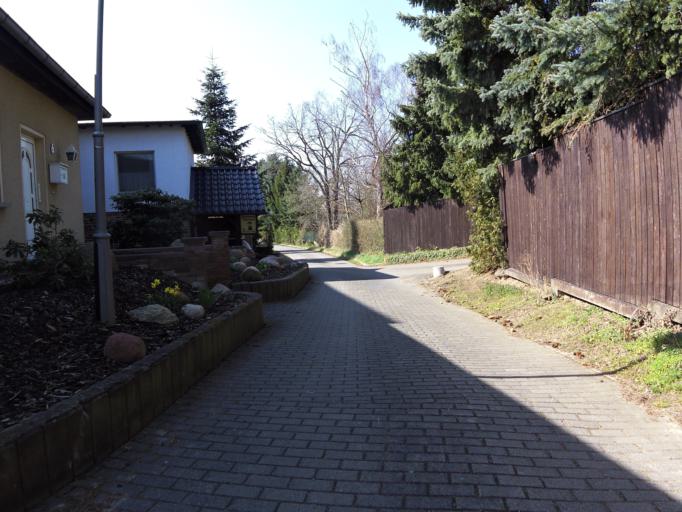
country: DE
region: Saxony
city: Leipzig
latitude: 51.3767
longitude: 12.3063
